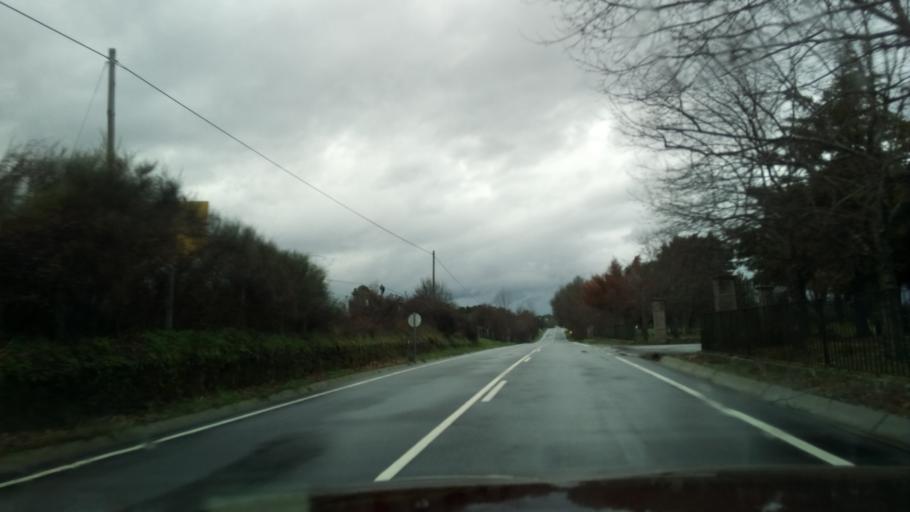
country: PT
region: Guarda
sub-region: Celorico da Beira
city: Celorico da Beira
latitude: 40.6210
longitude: -7.3157
